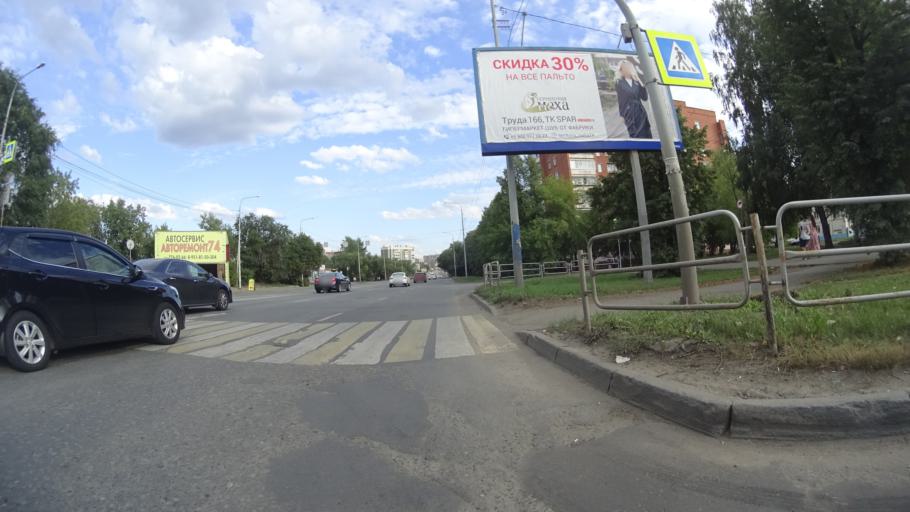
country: RU
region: Chelyabinsk
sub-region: Gorod Chelyabinsk
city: Chelyabinsk
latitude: 55.2021
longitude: 61.3266
